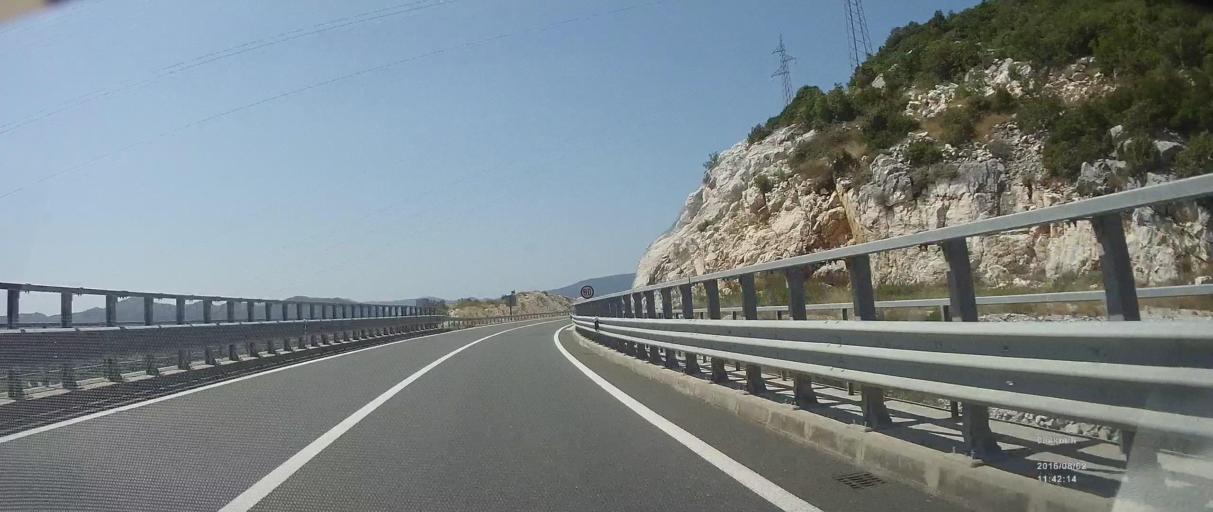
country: HR
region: Dubrovacko-Neretvanska
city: Komin
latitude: 43.0551
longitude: 17.4893
